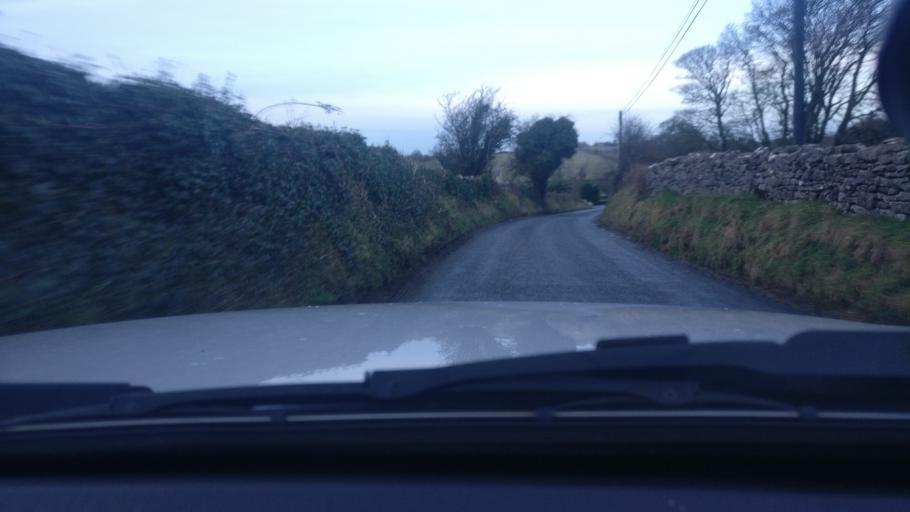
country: IE
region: Connaught
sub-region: County Galway
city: Loughrea
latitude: 53.1867
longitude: -8.6018
